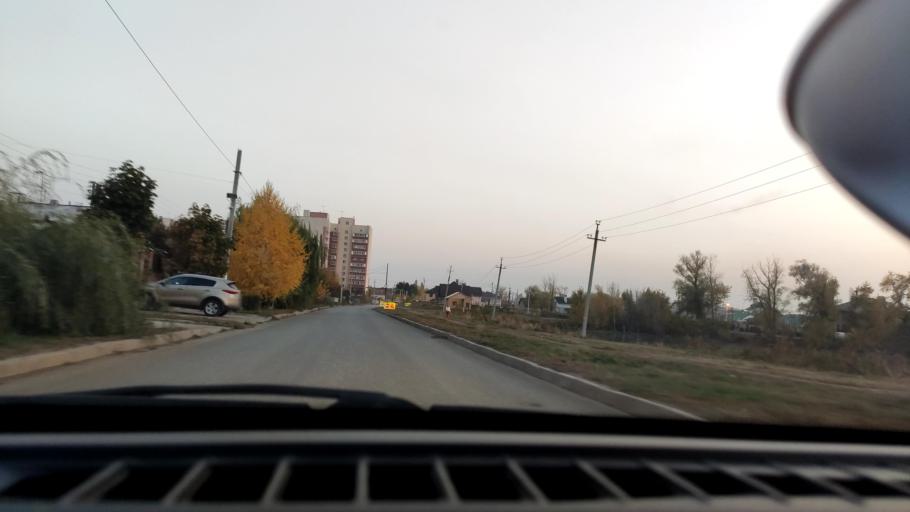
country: RU
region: Samara
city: Samara
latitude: 53.1529
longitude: 50.0882
